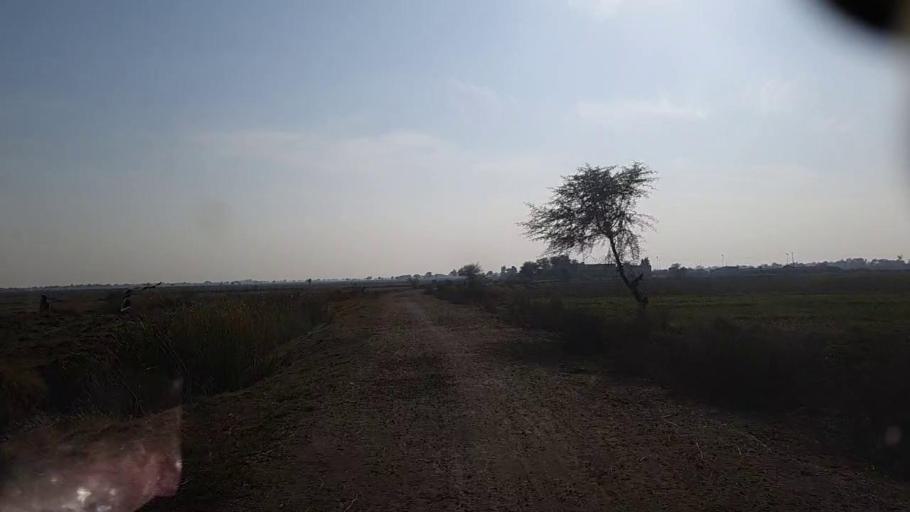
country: PK
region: Sindh
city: Jacobabad
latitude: 28.2923
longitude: 68.5575
